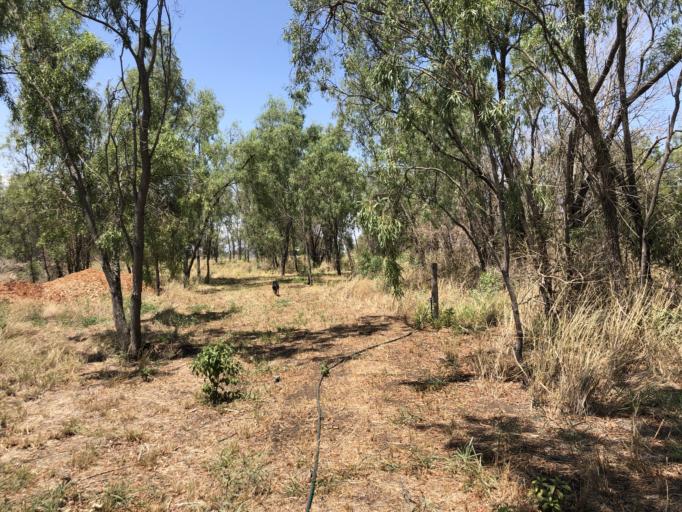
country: AU
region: Queensland
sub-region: Lockyer Valley
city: Gatton
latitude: -27.5861
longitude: 152.3466
